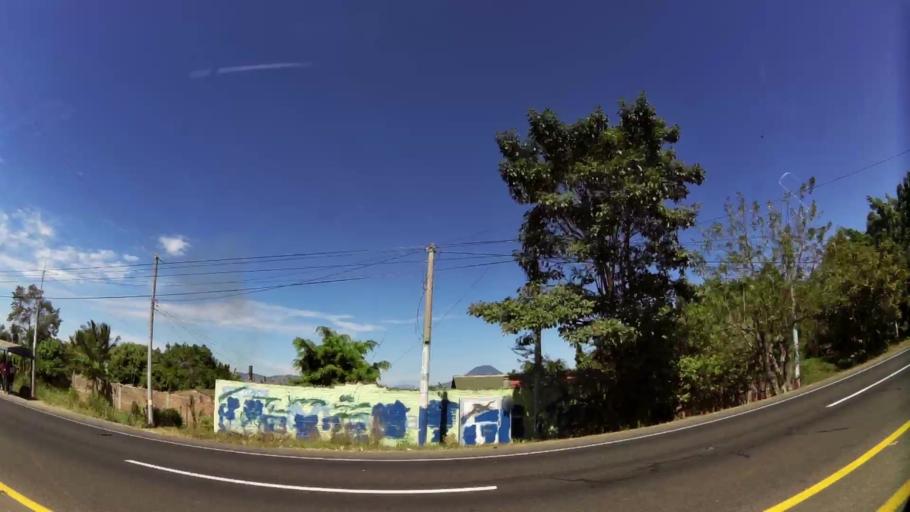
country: SV
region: Ahuachapan
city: Atiquizaya
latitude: 13.9715
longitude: -89.7400
